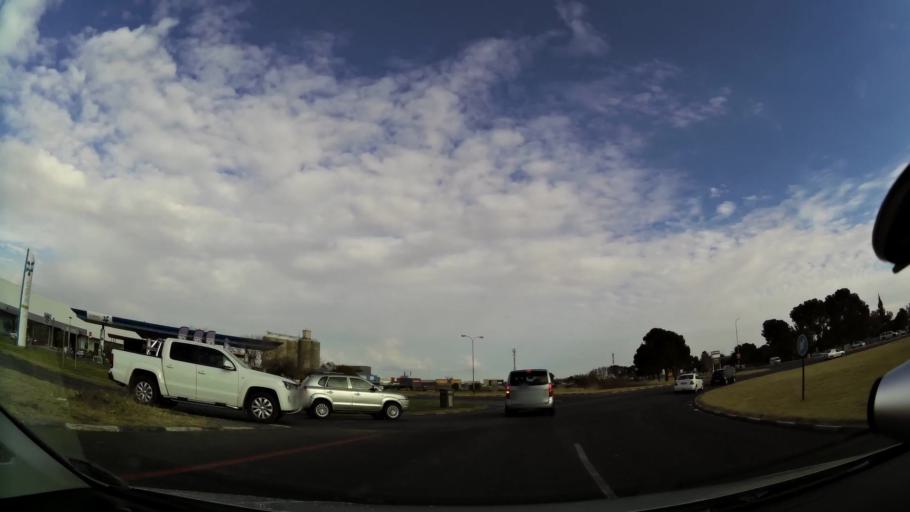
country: ZA
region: Orange Free State
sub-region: Lejweleputswa District Municipality
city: Welkom
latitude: -27.9814
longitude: 26.7614
